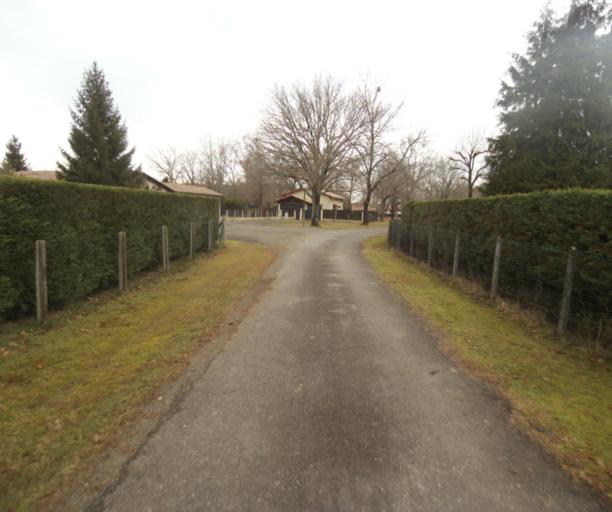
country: FR
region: Aquitaine
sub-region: Departement des Landes
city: Gabarret
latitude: 44.1017
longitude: -0.0178
